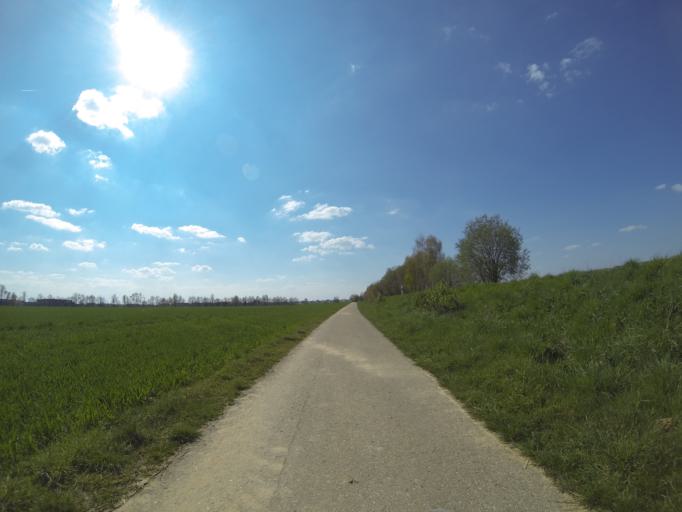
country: DE
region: Baden-Wuerttemberg
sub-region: Tuebingen Region
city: Burgrieden
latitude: 48.2292
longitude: 9.9175
